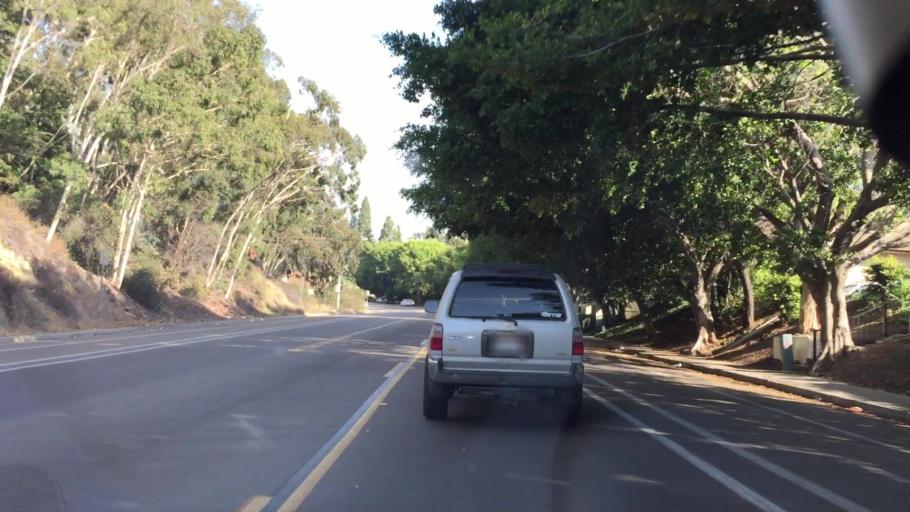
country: US
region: California
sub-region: San Diego County
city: Lemon Grove
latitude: 32.7625
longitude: -117.0831
